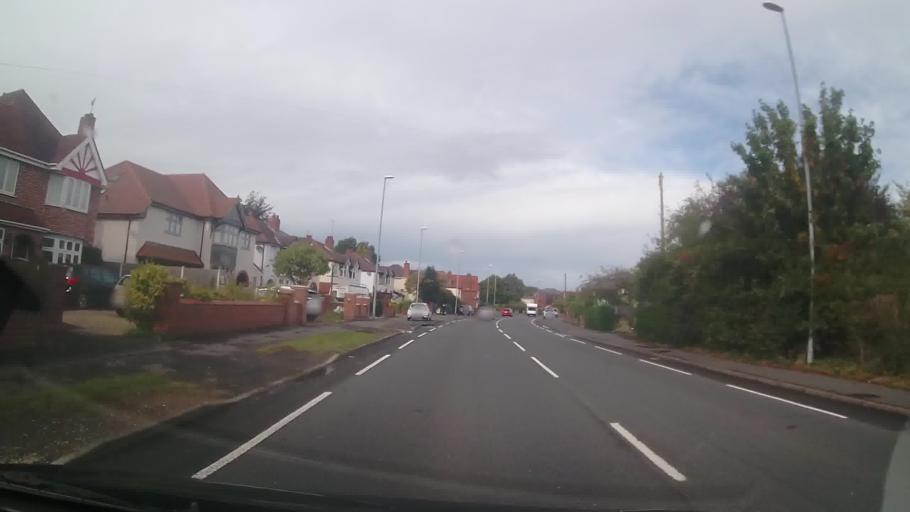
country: GB
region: England
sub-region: Worcestershire
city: Kidderminster
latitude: 52.3957
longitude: -2.2651
